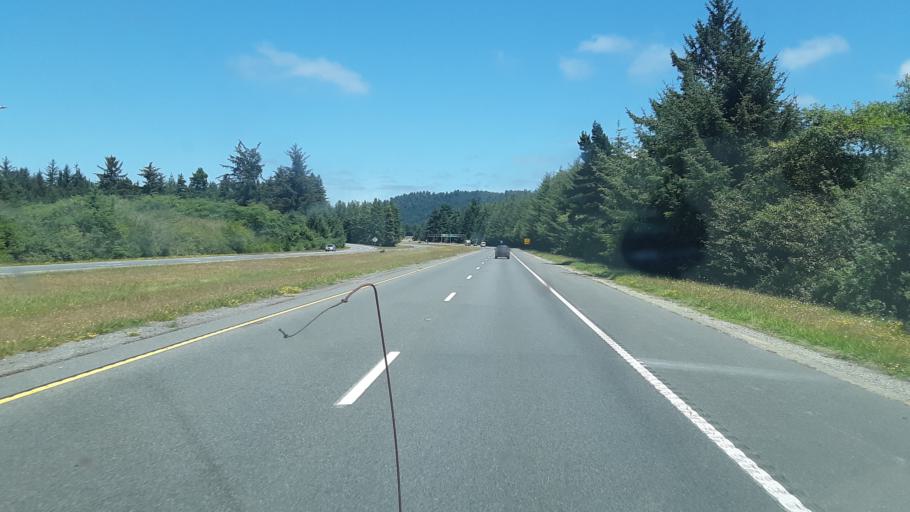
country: US
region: California
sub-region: Del Norte County
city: Bertsch-Oceanview
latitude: 41.7958
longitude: -124.1557
